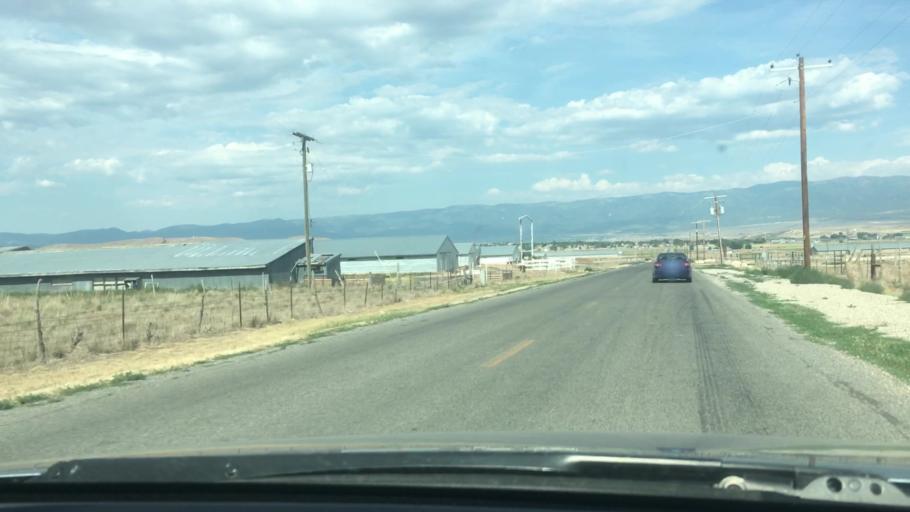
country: US
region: Utah
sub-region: Sanpete County
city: Moroni
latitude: 39.5235
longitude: -111.6306
